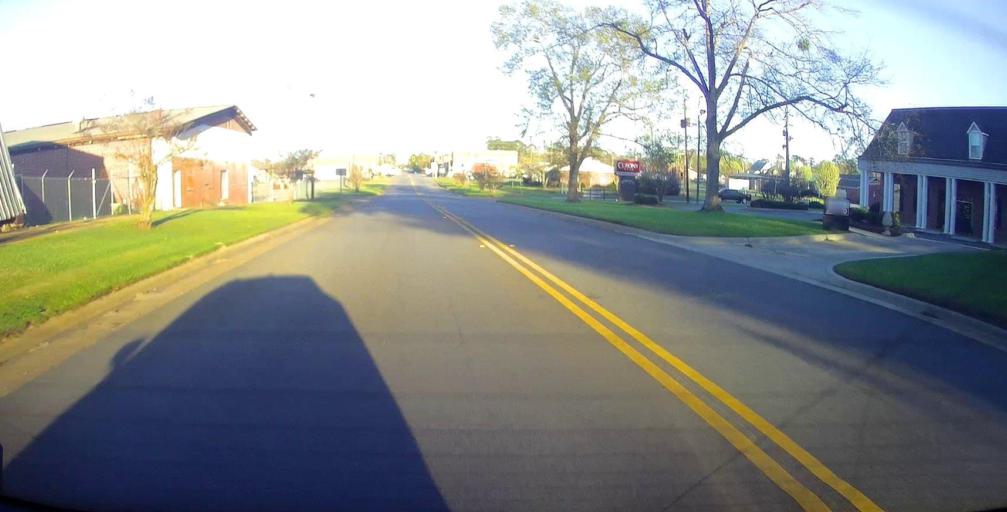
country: US
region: Georgia
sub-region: Wilcox County
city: Rochelle
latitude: 31.9509
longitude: -83.4585
